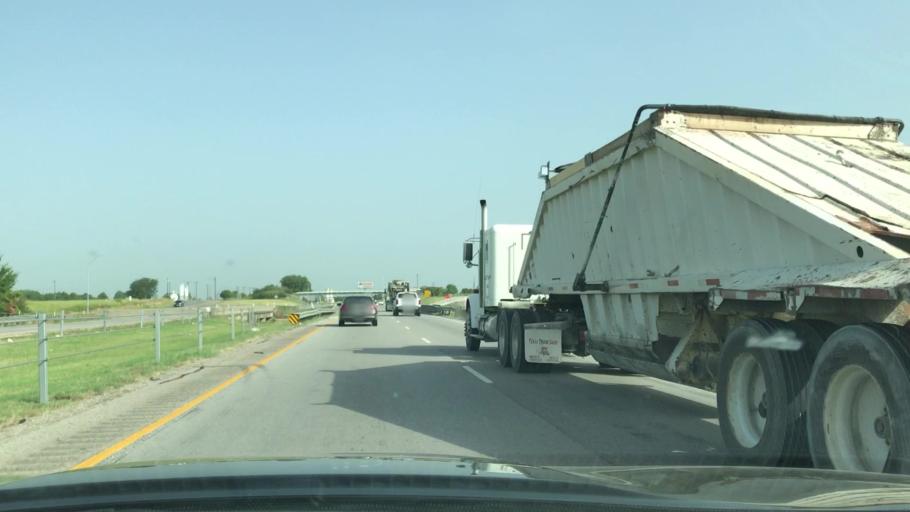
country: US
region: Texas
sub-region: Kaufman County
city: Forney
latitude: 32.7665
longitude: -96.4850
